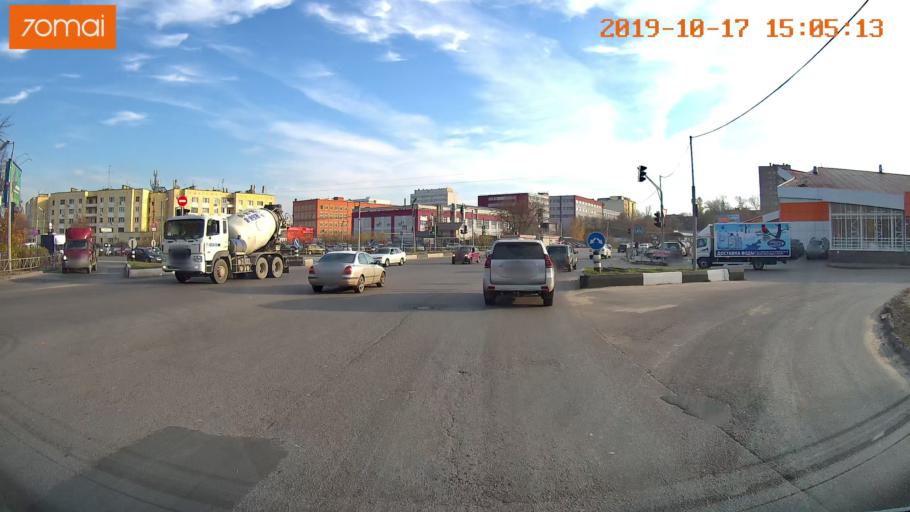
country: RU
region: Rjazan
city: Ryazan'
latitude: 54.6372
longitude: 39.7227
